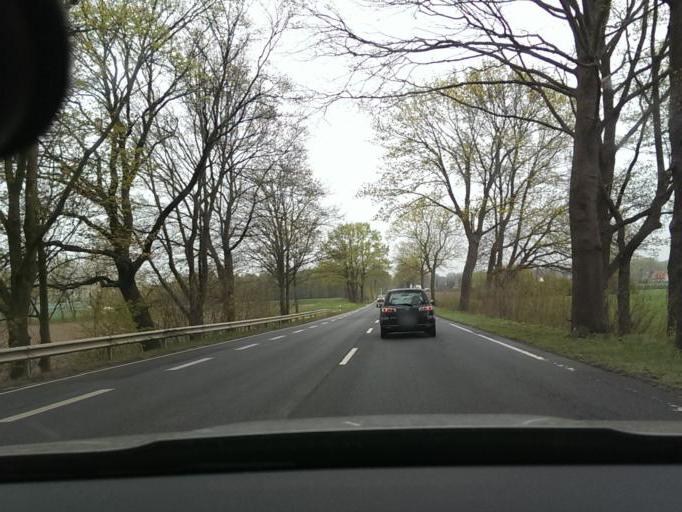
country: DE
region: Lower Saxony
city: Elze
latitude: 52.5569
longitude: 9.7241
